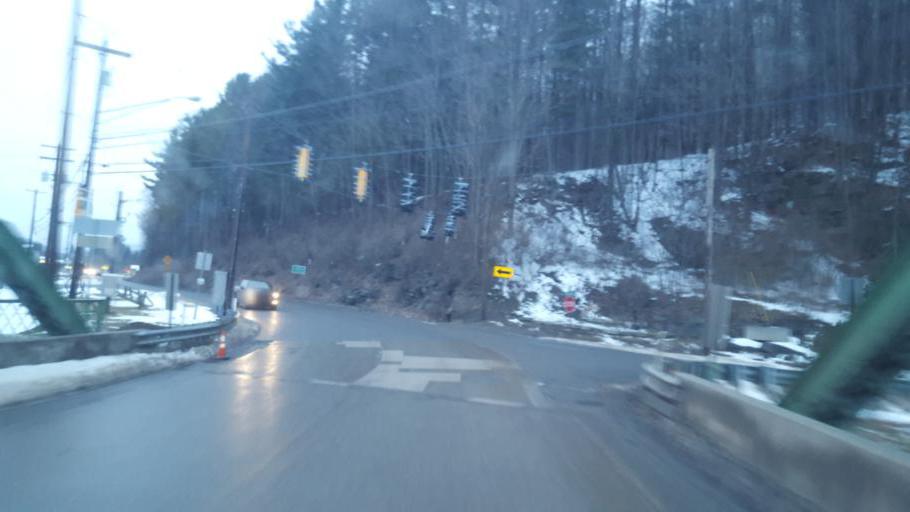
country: US
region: Pennsylvania
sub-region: Potter County
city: Coudersport
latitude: 41.7699
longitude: -78.0251
